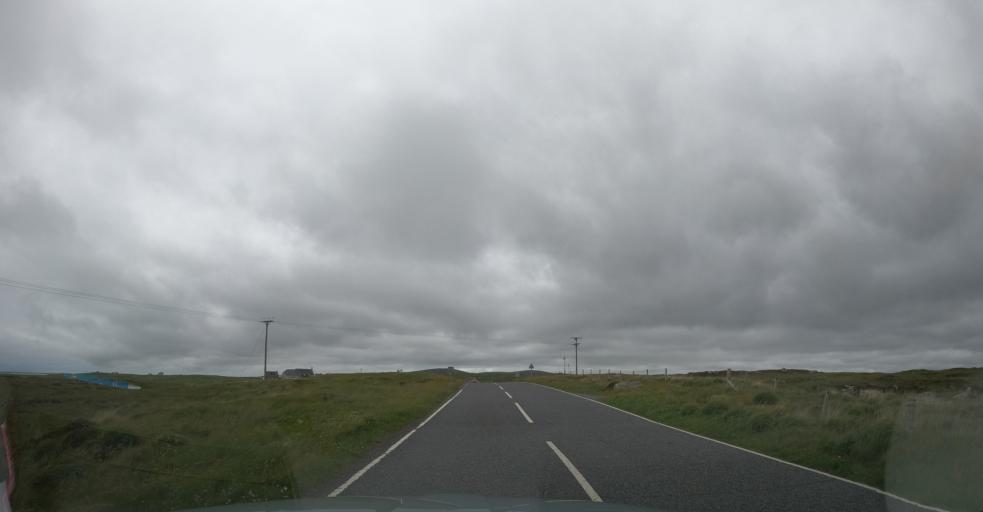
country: GB
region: Scotland
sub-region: Eilean Siar
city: Isle of North Uist
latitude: 57.5483
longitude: -7.3280
